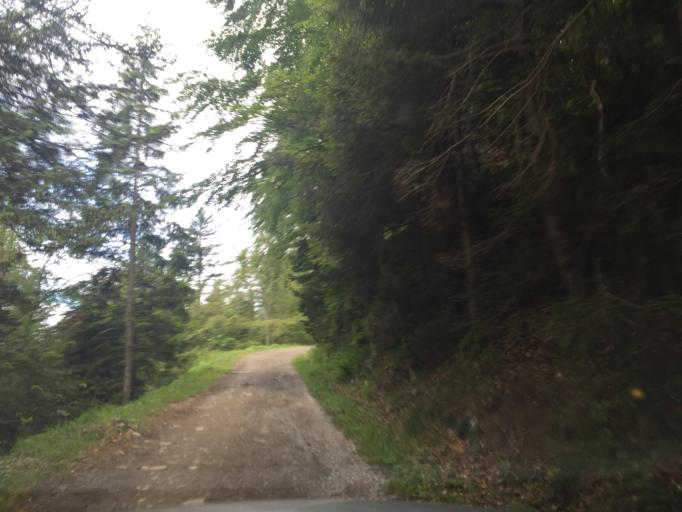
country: FR
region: Rhone-Alpes
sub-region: Departement de la Savoie
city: La Rochette
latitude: 45.4404
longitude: 6.1681
